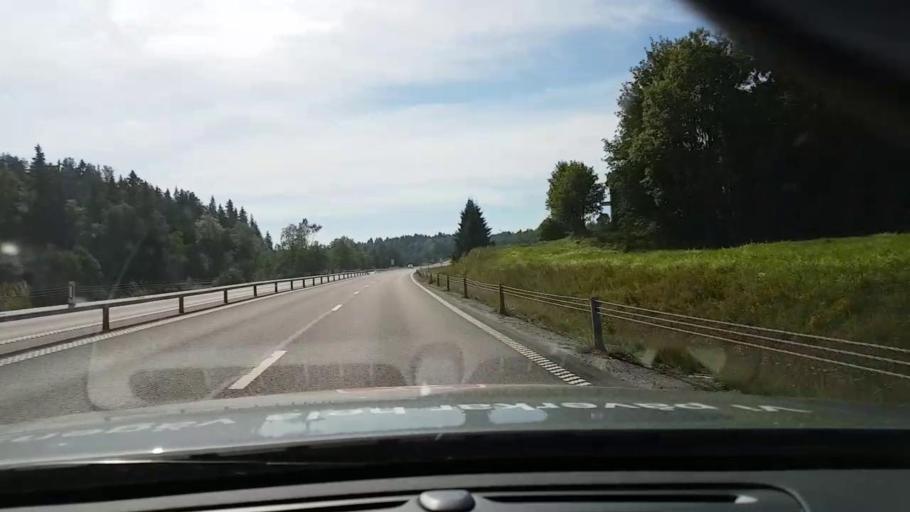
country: SE
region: Vaesternorrland
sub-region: OErnskoeldsviks Kommun
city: Husum
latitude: 63.3562
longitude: 19.1673
